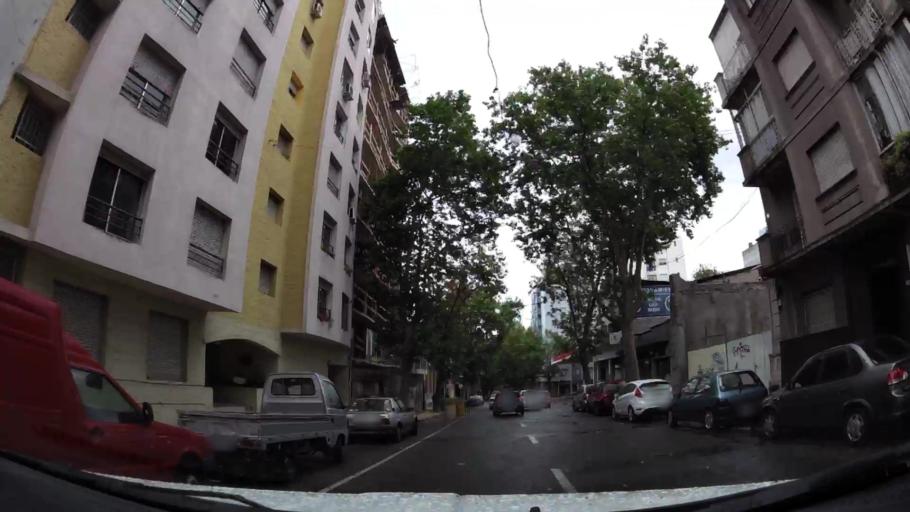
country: UY
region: Montevideo
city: Montevideo
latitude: -34.9086
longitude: -56.1890
